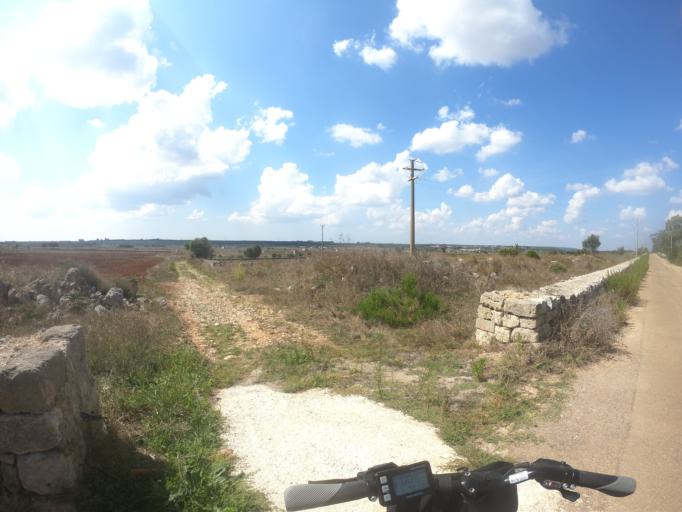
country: IT
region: Apulia
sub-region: Provincia di Lecce
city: Specchia
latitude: 39.9492
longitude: 18.2669
